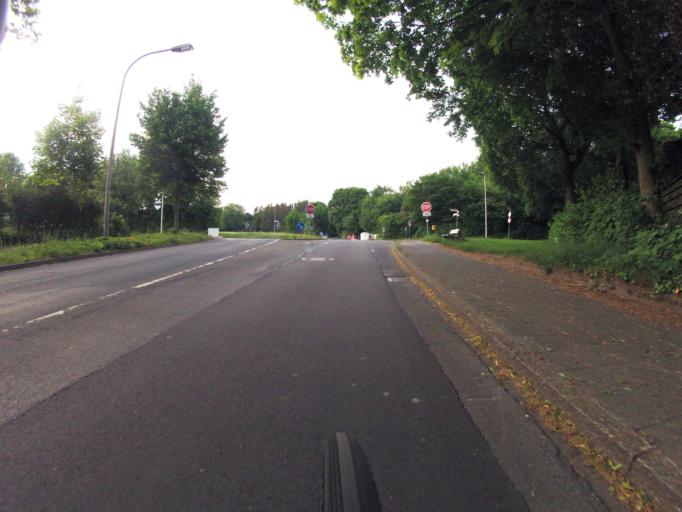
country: DE
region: North Rhine-Westphalia
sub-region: Regierungsbezirk Munster
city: Mettingen
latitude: 52.2728
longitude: 7.7739
